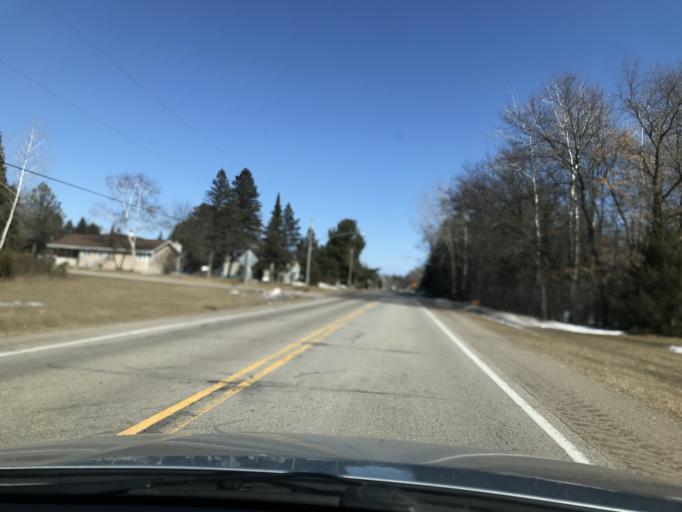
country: US
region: Wisconsin
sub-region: Marinette County
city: Peshtigo
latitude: 45.2391
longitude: -88.0178
